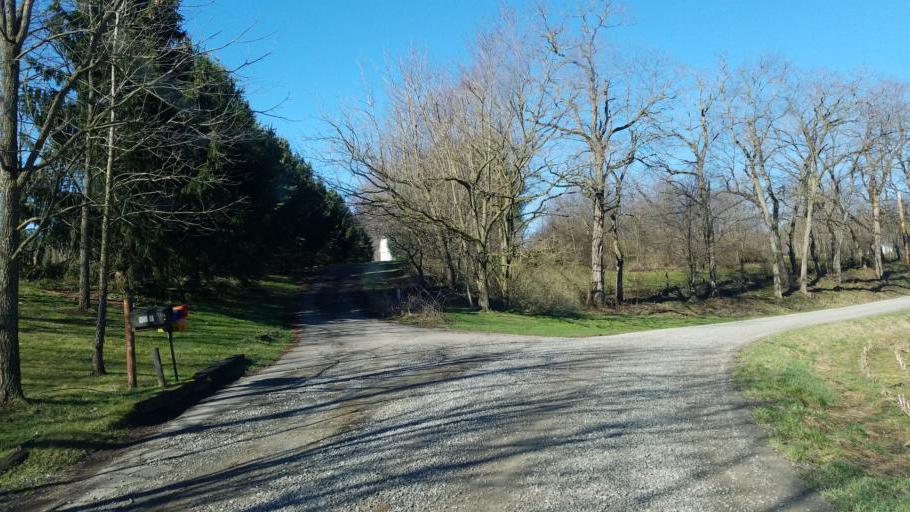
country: US
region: Ohio
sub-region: Wayne County
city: Apple Creek
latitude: 40.6642
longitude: -81.8251
